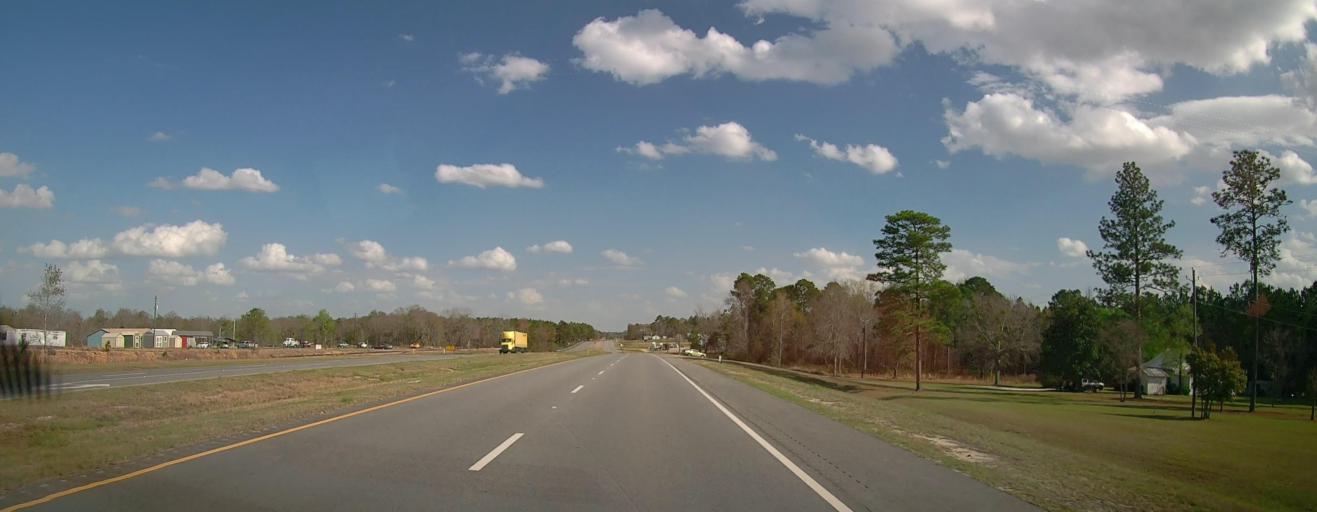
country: US
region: Georgia
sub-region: Telfair County
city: Helena
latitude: 32.0852
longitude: -82.9315
